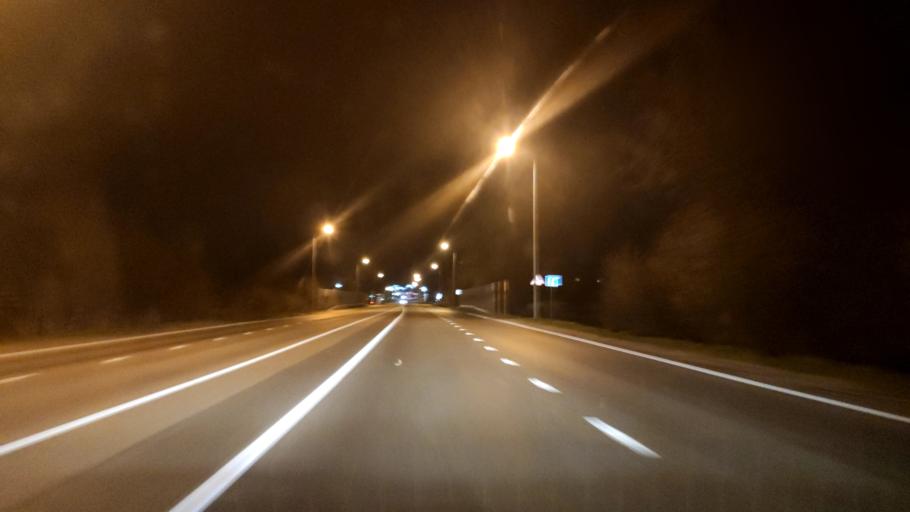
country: RU
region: Belgorod
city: Staryy Oskol
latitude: 51.3521
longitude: 37.8294
